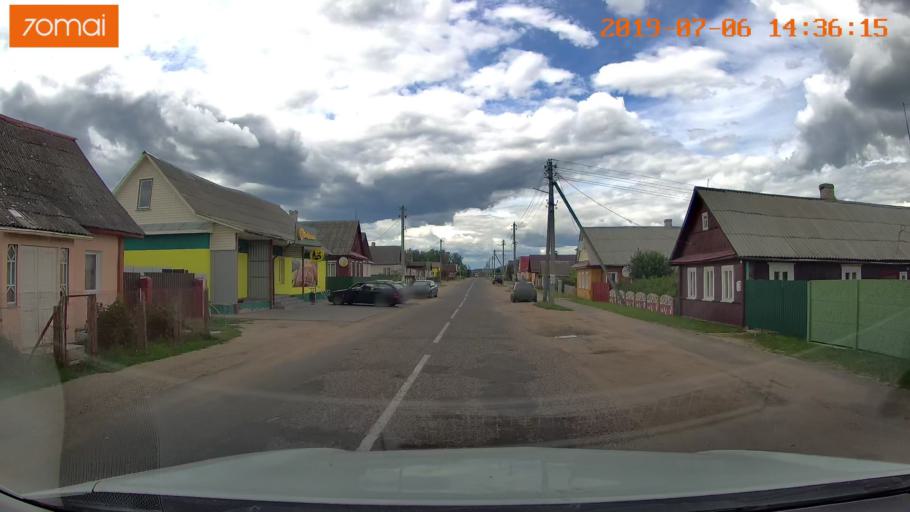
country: BY
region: Minsk
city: Ivyanyets
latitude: 53.8897
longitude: 26.7328
